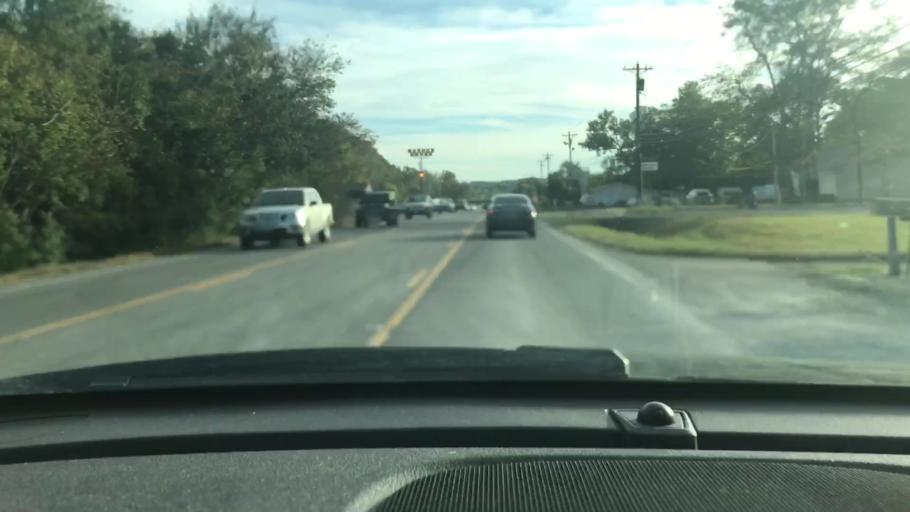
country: US
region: Tennessee
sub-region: Sumner County
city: Millersville
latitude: 36.3538
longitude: -86.7144
